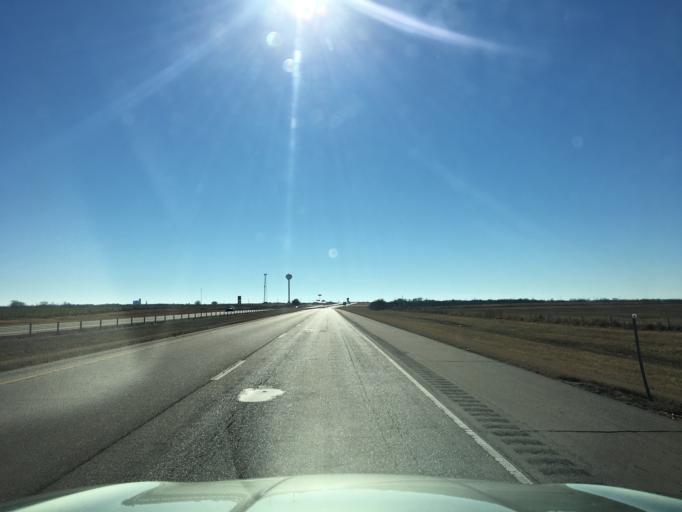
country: US
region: Oklahoma
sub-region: Kay County
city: Blackwell
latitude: 36.9519
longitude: -97.3458
